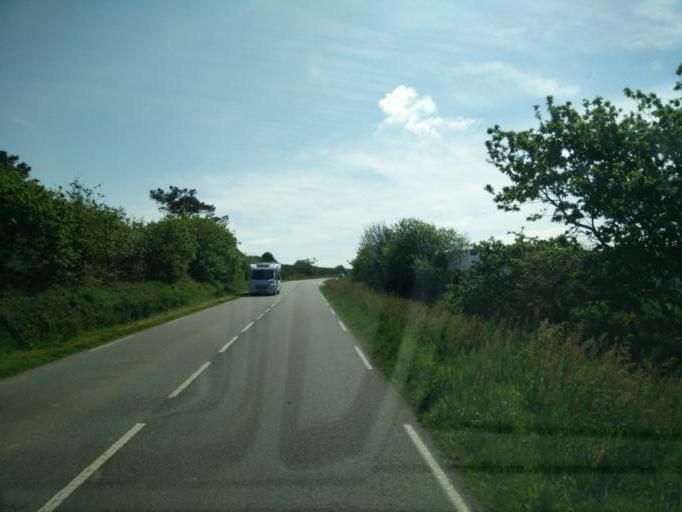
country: FR
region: Brittany
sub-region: Departement du Finistere
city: Plomodiern
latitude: 48.2252
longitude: -4.2640
